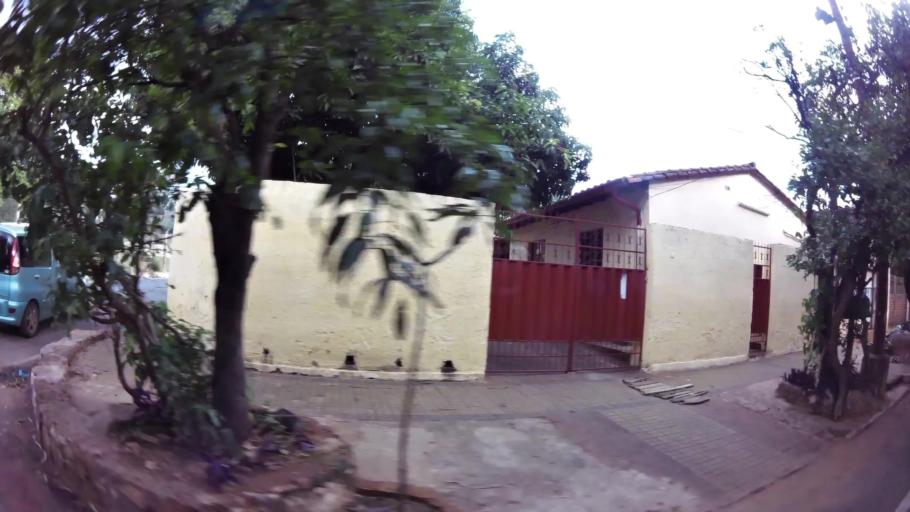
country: PY
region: Central
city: Fernando de la Mora
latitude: -25.3384
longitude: -57.5614
